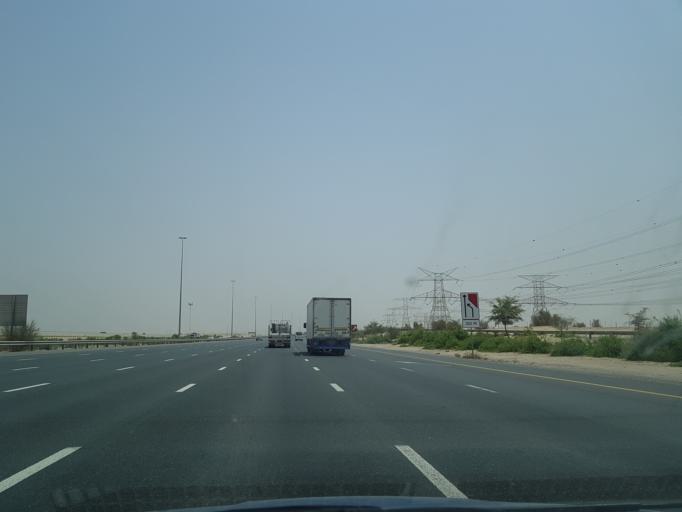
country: AE
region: Dubai
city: Dubai
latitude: 25.0551
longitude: 55.3156
